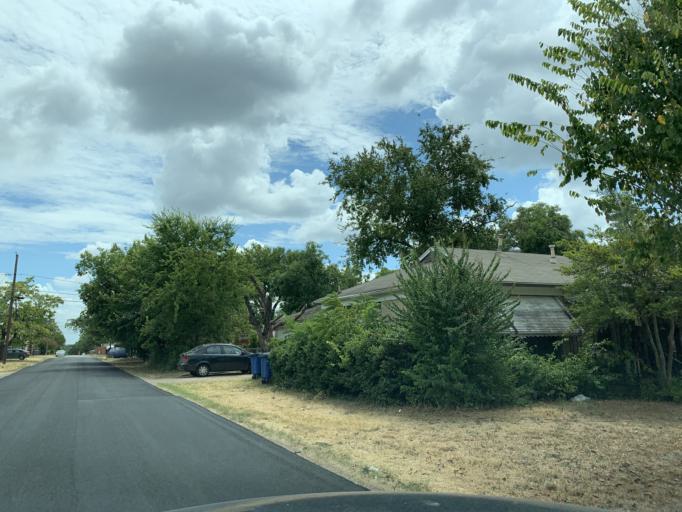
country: US
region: Texas
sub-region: Dallas County
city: Cockrell Hill
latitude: 32.7515
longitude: -96.8713
